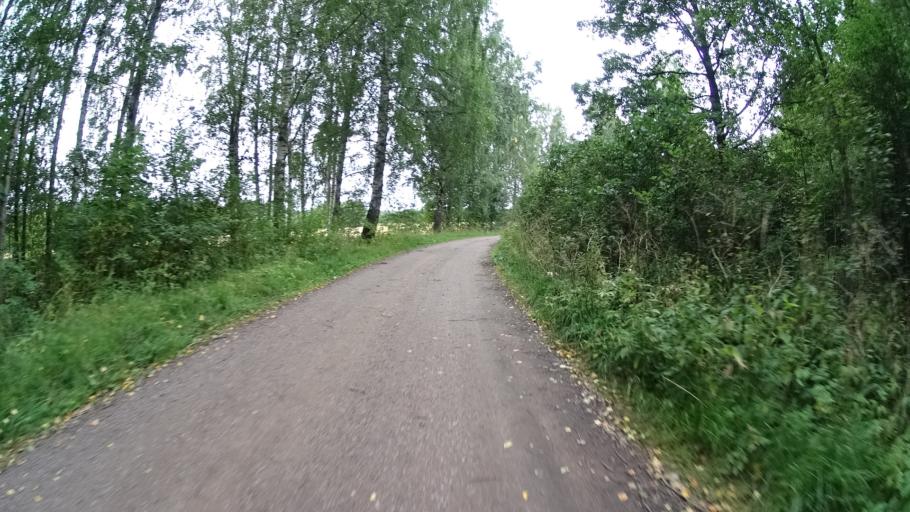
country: FI
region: Uusimaa
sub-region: Helsinki
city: Teekkarikylae
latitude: 60.2700
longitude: 24.8893
